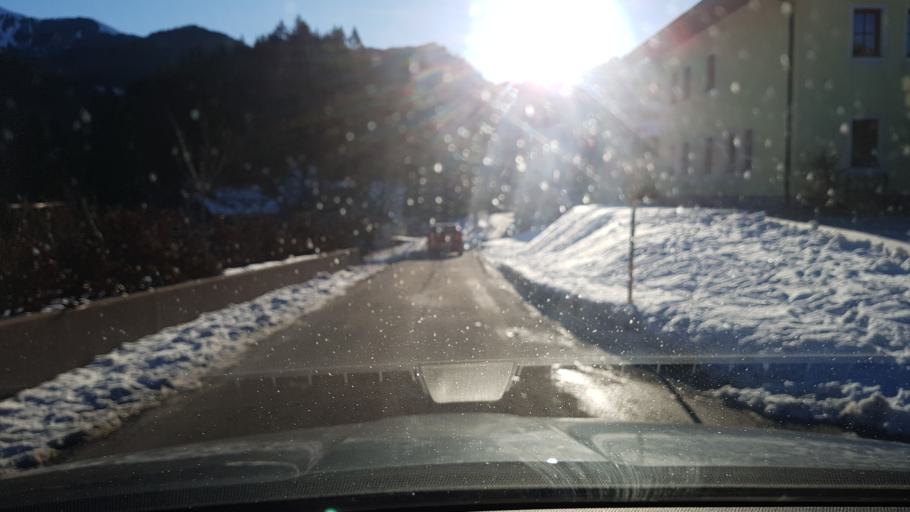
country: AT
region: Salzburg
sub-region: Politischer Bezirk Hallein
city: Scheffau am Tennengebirge
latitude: 47.6505
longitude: 13.2157
